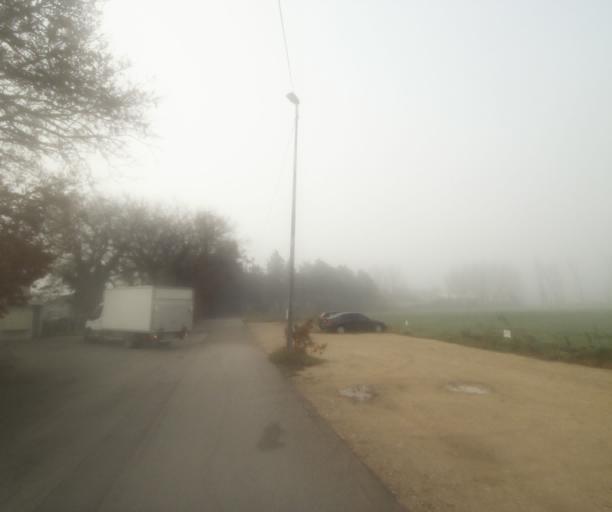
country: FR
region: Provence-Alpes-Cote d'Azur
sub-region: Departement des Bouches-du-Rhone
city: Eguilles
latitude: 43.5460
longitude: 5.3570
